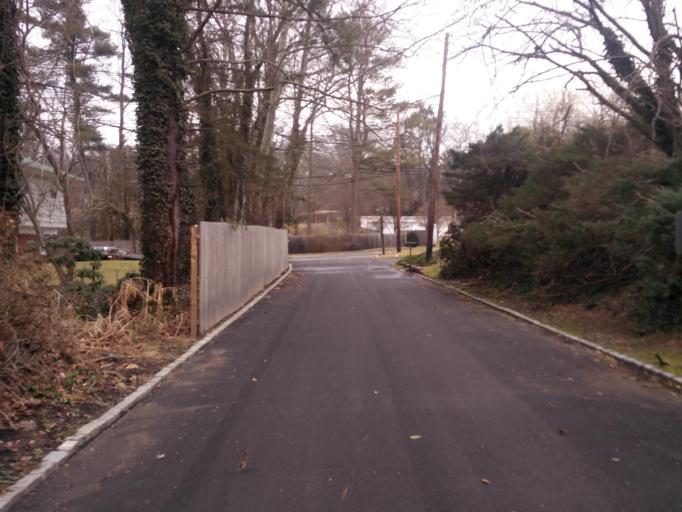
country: US
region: New York
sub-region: Nassau County
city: Locust Valley
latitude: 40.8779
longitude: -73.5794
